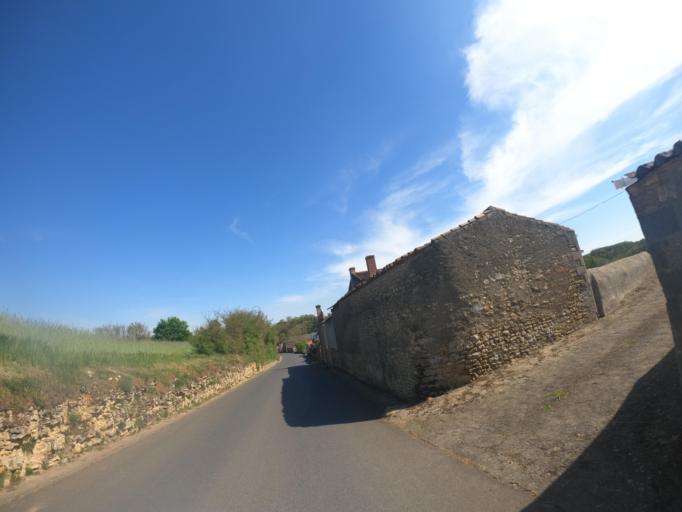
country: FR
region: Poitou-Charentes
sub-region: Departement des Deux-Sevres
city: Airvault
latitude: 46.8850
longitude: -0.1439
